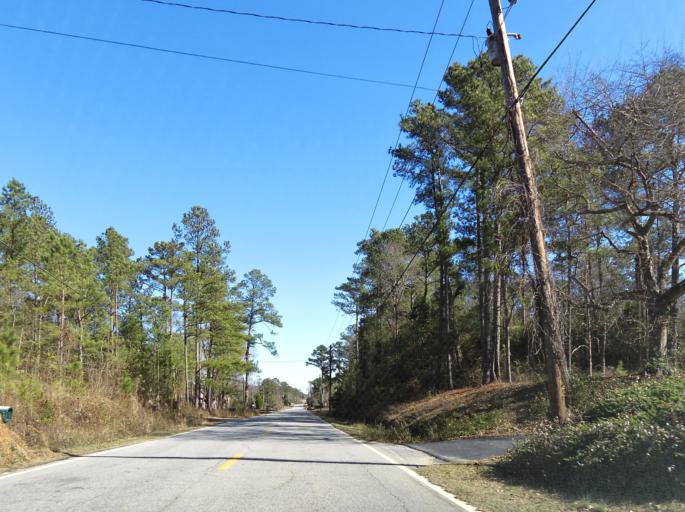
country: US
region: Georgia
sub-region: Bibb County
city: West Point
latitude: 32.8049
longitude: -83.7975
